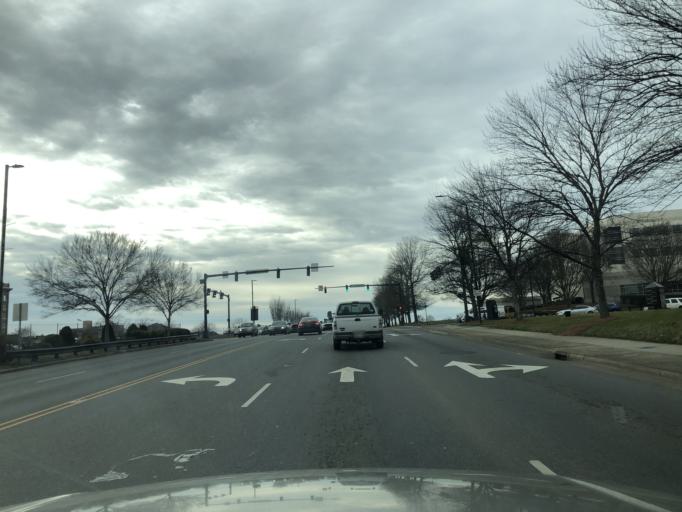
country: US
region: North Carolina
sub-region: Gaston County
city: Gastonia
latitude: 35.2656
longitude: -81.1811
